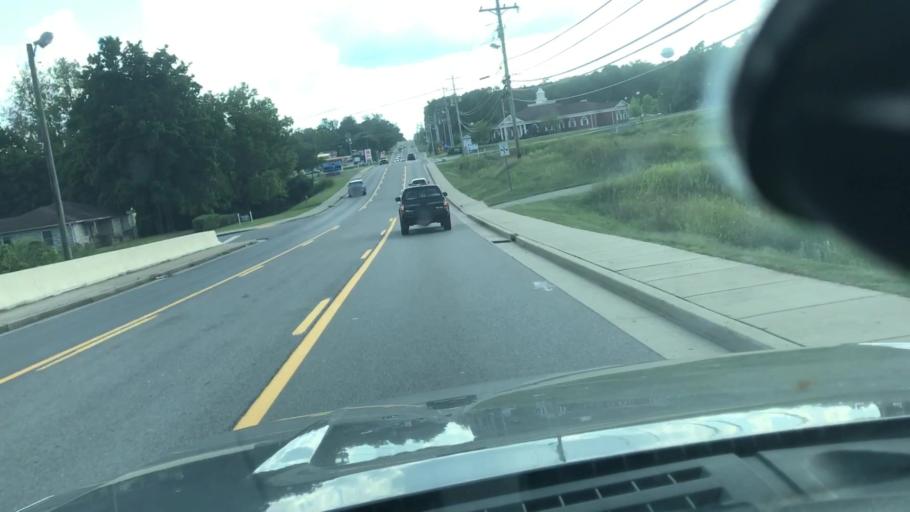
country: US
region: Tennessee
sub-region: Williamson County
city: Fairview
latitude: 35.9759
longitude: -87.1268
